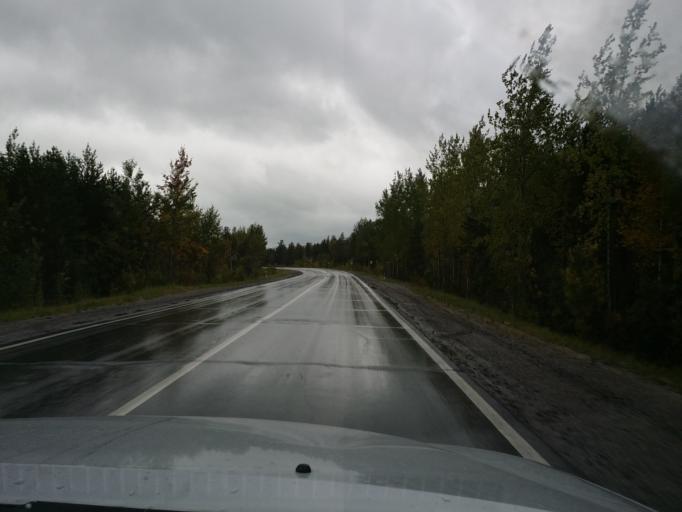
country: RU
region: Khanty-Mansiyskiy Avtonomnyy Okrug
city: Megion
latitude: 61.1031
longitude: 75.8544
